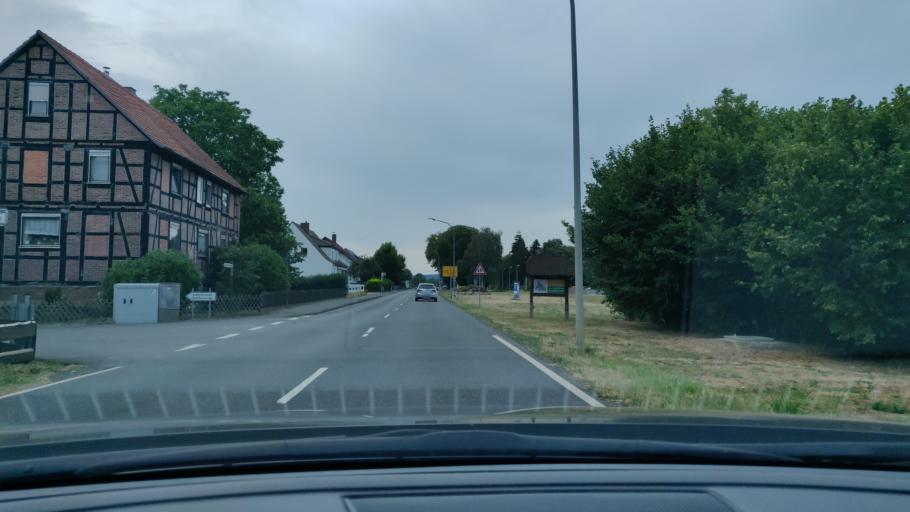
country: DE
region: Hesse
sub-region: Regierungsbezirk Kassel
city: Wabern
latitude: 51.1112
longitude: 9.3199
